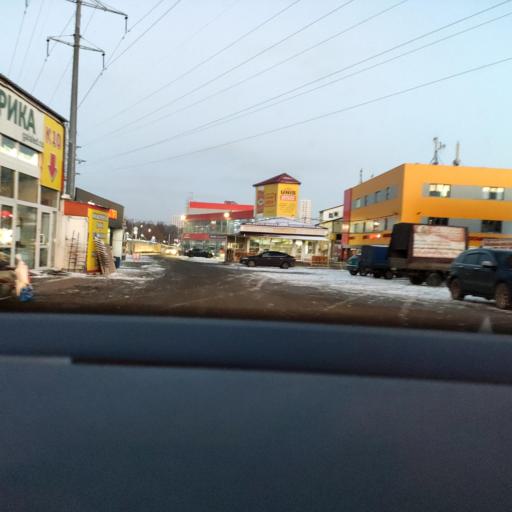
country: RU
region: Moskovskaya
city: Reutov
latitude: 55.7769
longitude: 37.8541
